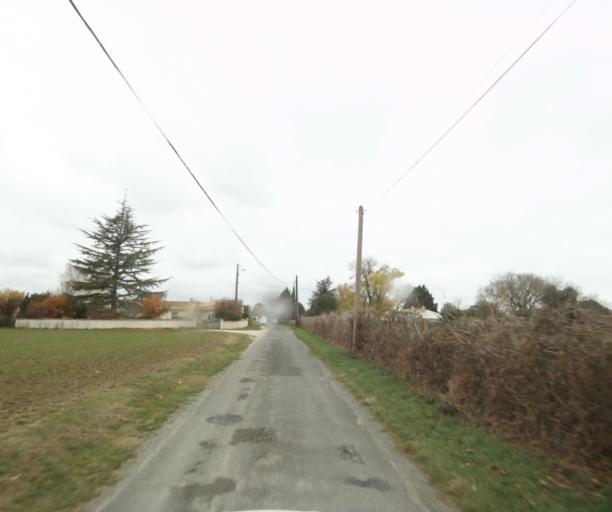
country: FR
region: Poitou-Charentes
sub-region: Departement de la Charente-Maritime
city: Bussac-sur-Charente
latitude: 45.7679
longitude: -0.6317
